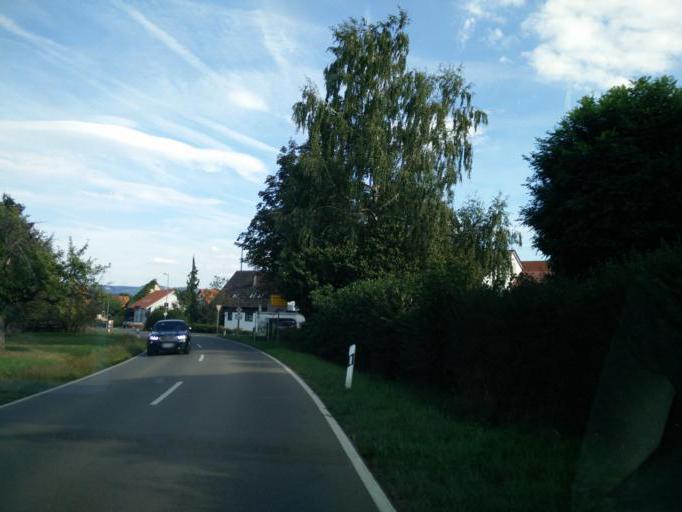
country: DE
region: Baden-Wuerttemberg
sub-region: Tuebingen Region
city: Sickenhausen
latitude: 48.5245
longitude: 9.1718
